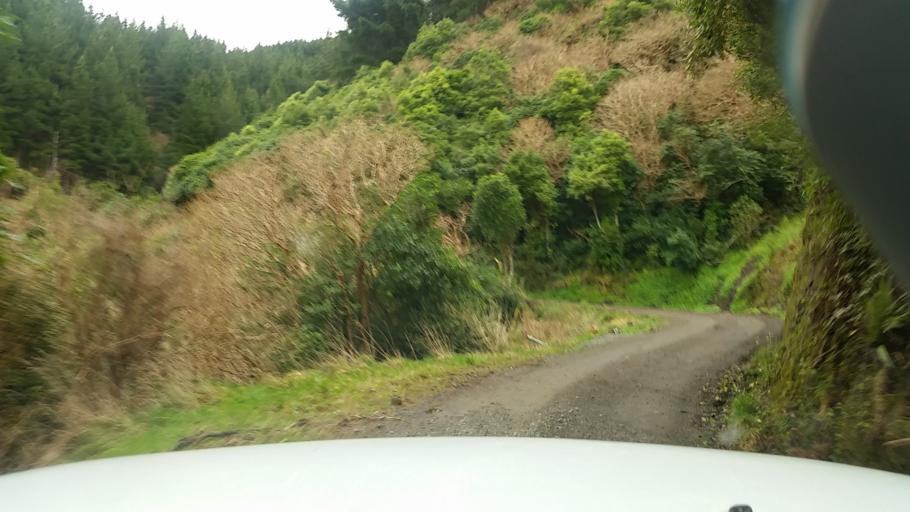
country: NZ
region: Canterbury
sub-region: Christchurch City
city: Christchurch
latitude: -43.7033
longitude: 172.7756
